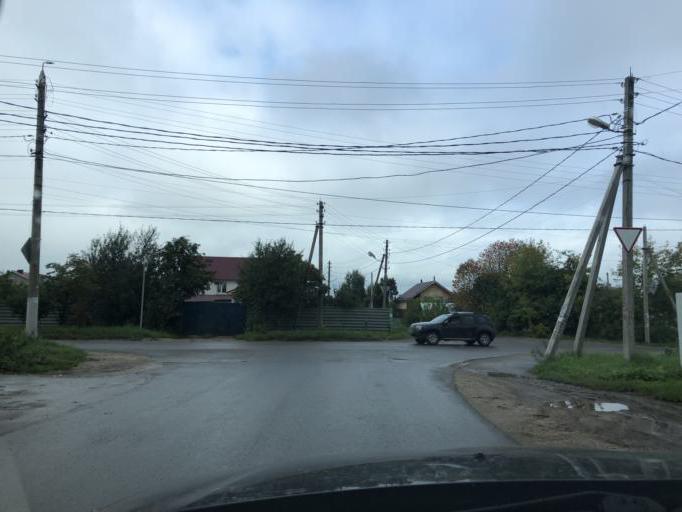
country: RU
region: Tula
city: Mendeleyevskiy
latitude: 54.1788
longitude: 37.5507
